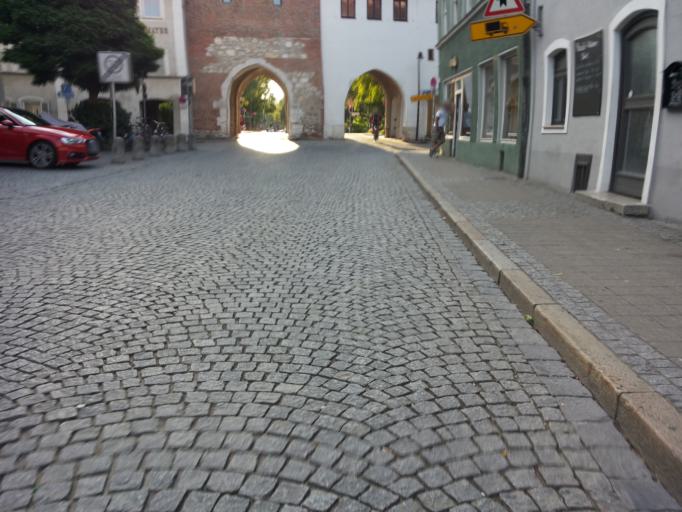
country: DE
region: Bavaria
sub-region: Upper Bavaria
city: Ingolstadt
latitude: 48.7641
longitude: 11.4185
